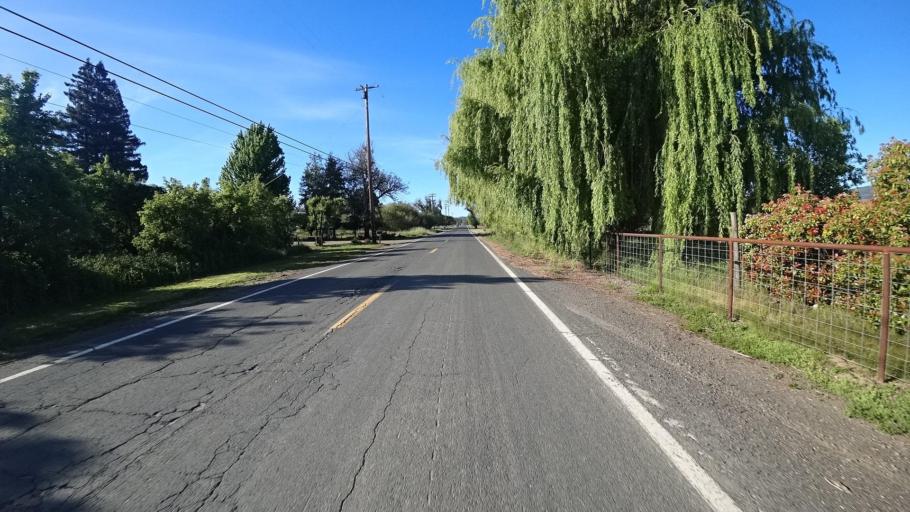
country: US
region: California
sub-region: Lake County
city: Lakeport
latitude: 39.0738
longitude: -122.9498
